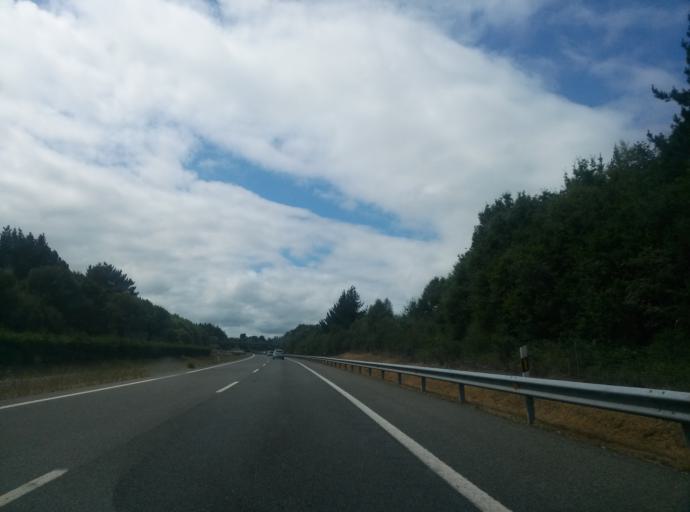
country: ES
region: Galicia
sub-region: Provincia de Lugo
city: Rabade
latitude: 43.1378
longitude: -7.6403
